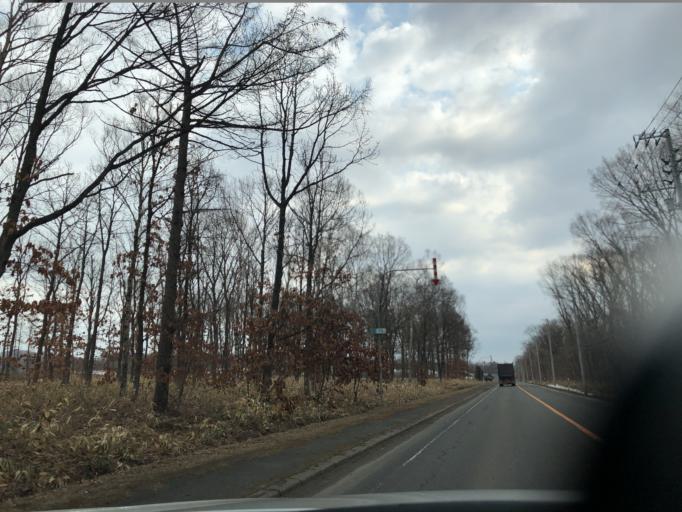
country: JP
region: Hokkaido
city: Chitose
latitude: 42.7613
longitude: 141.7781
